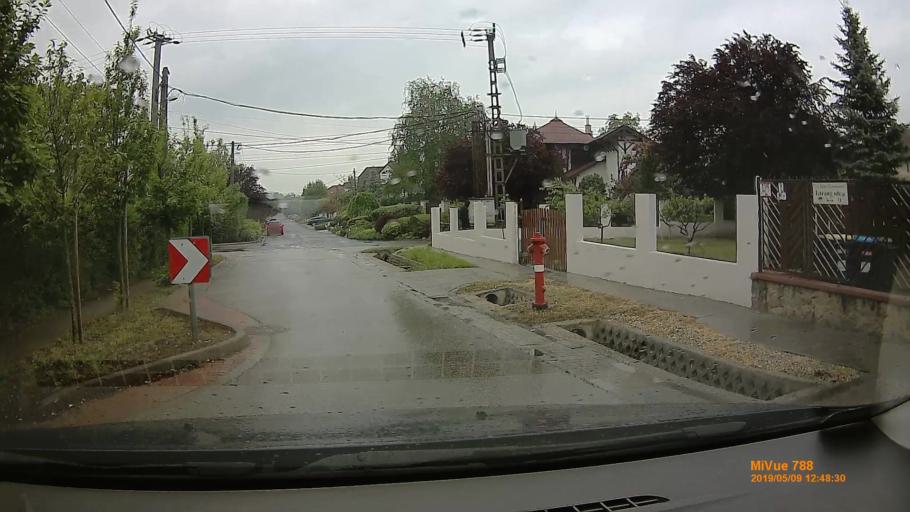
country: HU
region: Budapest
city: Budapest XVI. keruelet
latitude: 47.5381
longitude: 19.1810
